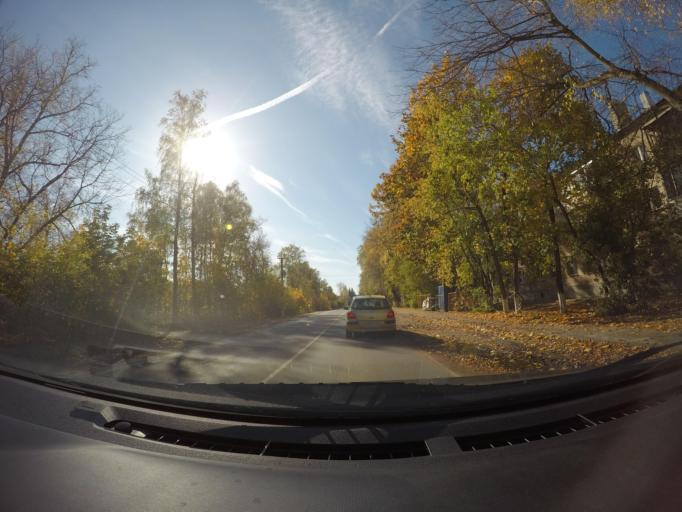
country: RU
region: Moskovskaya
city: Rodniki
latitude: 55.6480
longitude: 38.0550
